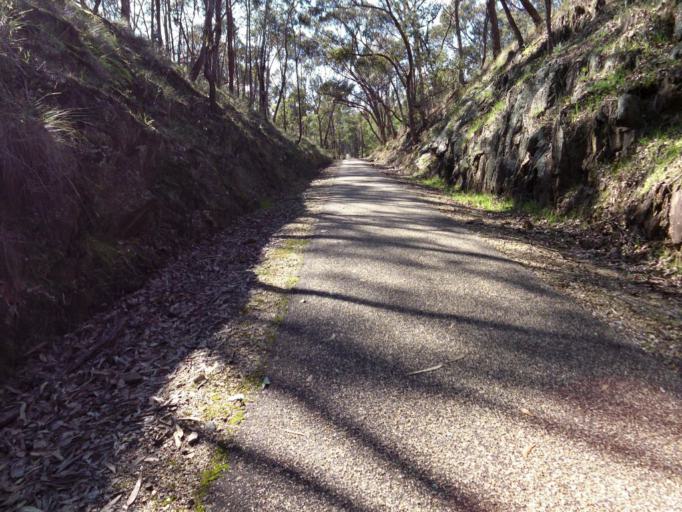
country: AU
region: Victoria
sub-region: Wangaratta
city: Wangaratta
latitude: -36.4048
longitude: 146.6271
